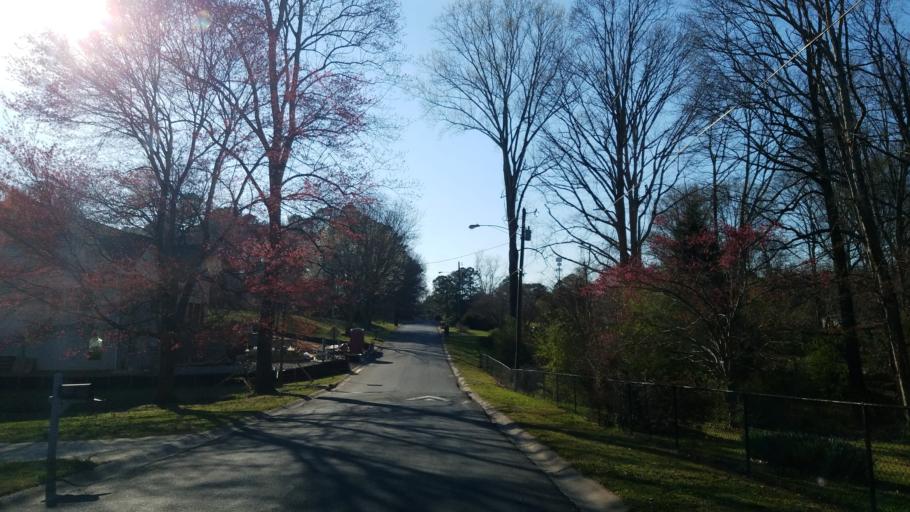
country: US
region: Georgia
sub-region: Cobb County
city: Marietta
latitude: 33.9999
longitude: -84.4964
